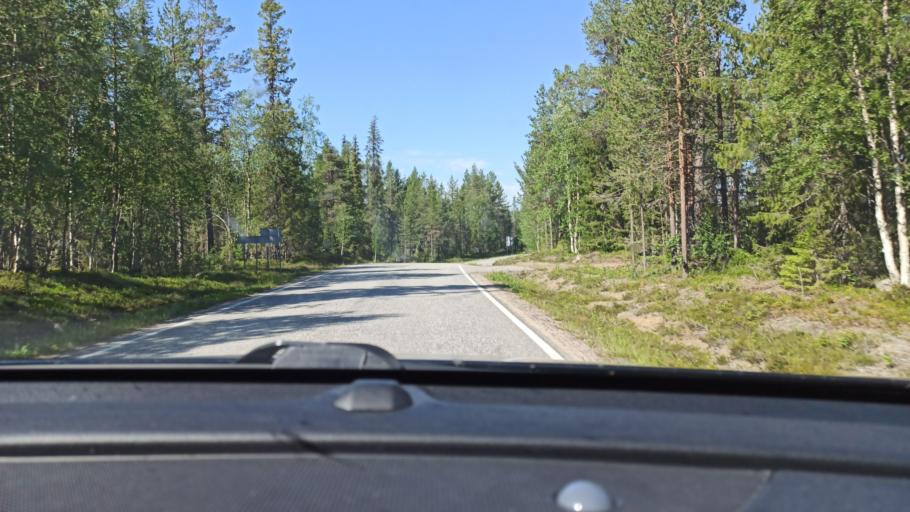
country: FI
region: Lapland
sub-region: Tunturi-Lappi
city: Kolari
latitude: 67.6842
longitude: 24.1071
